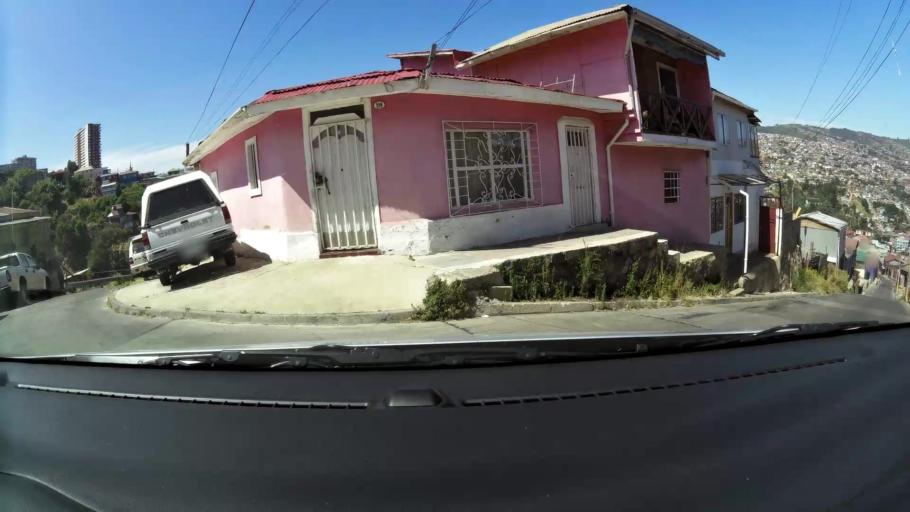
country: CL
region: Valparaiso
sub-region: Provincia de Valparaiso
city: Valparaiso
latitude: -33.0508
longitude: -71.5952
